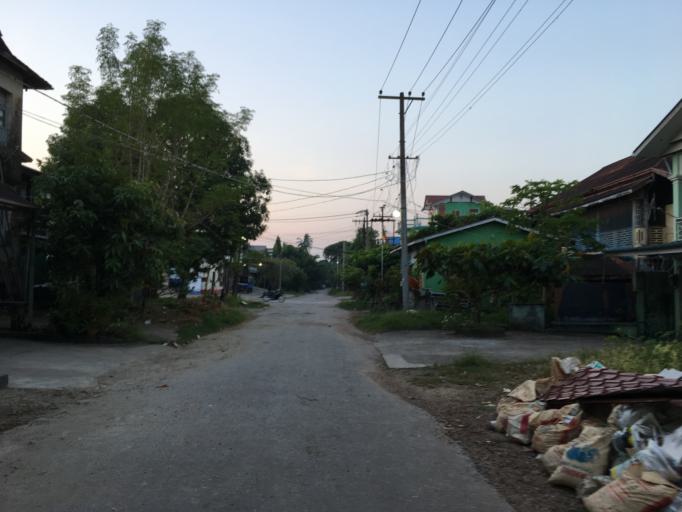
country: MM
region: Mon
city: Mawlamyine
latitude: 16.4775
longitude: 97.6213
